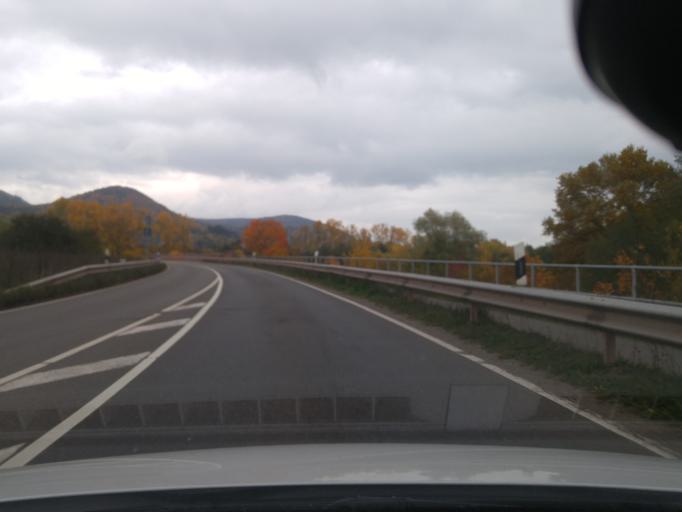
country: DE
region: Rheinland-Pfalz
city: Albersweiler
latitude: 49.2172
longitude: 8.0033
